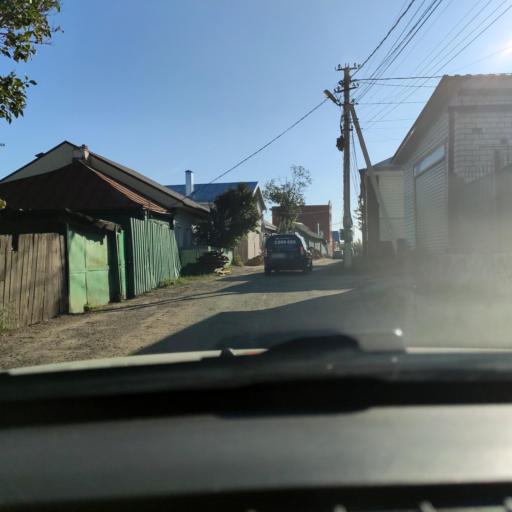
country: RU
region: Voronezj
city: Voronezh
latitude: 51.6333
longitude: 39.2020
